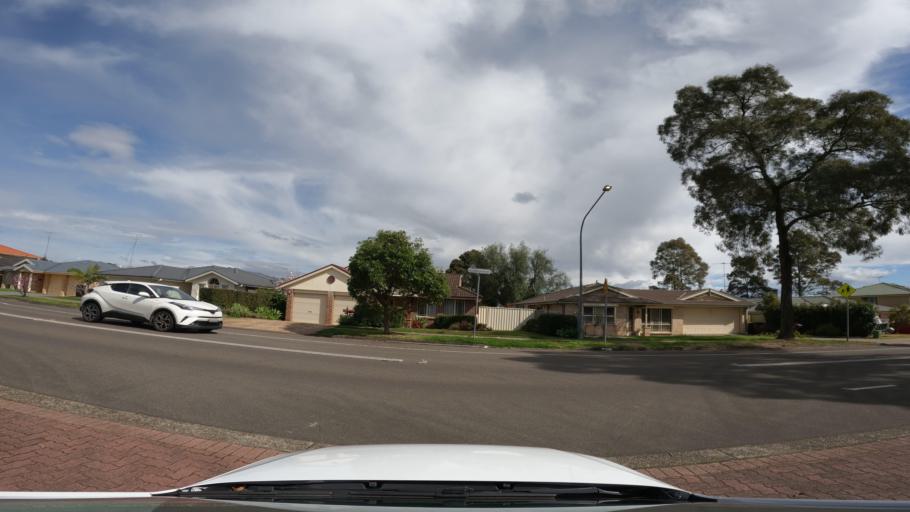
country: AU
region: New South Wales
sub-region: Blacktown
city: Stanhope Gardens
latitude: -33.7282
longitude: 150.9390
